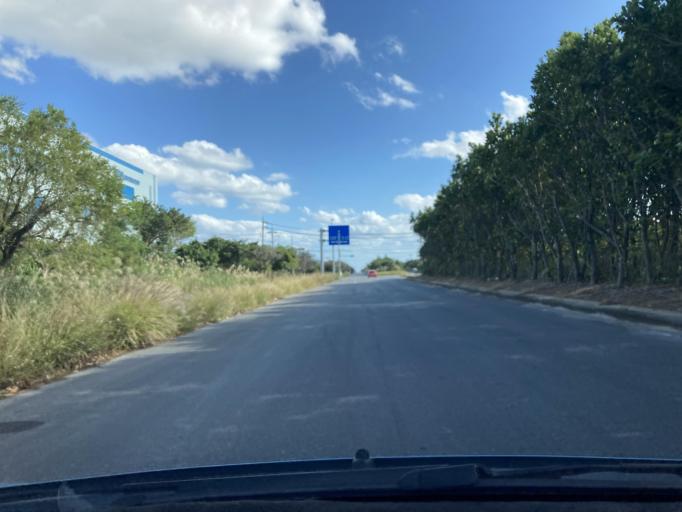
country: JP
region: Okinawa
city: Katsuren-haebaru
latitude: 26.3364
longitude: 127.8632
